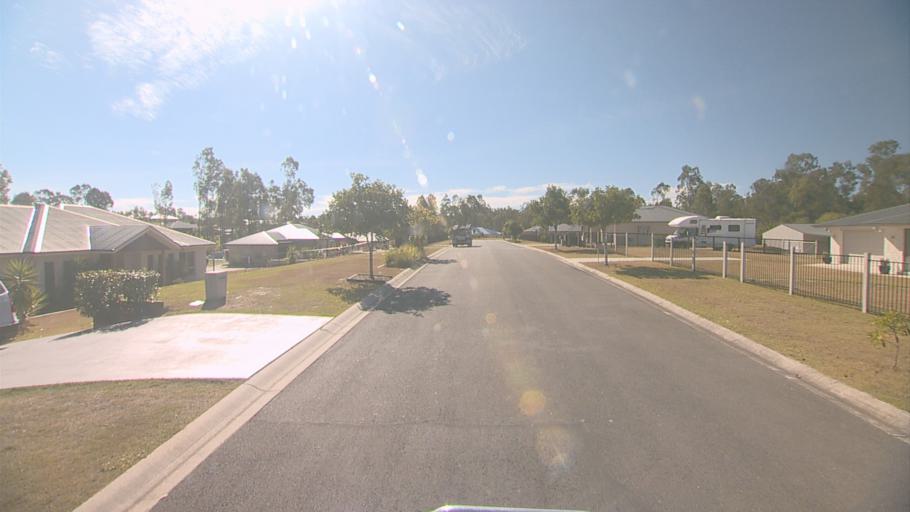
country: AU
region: Queensland
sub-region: Logan
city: North Maclean
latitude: -27.8295
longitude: 152.9849
